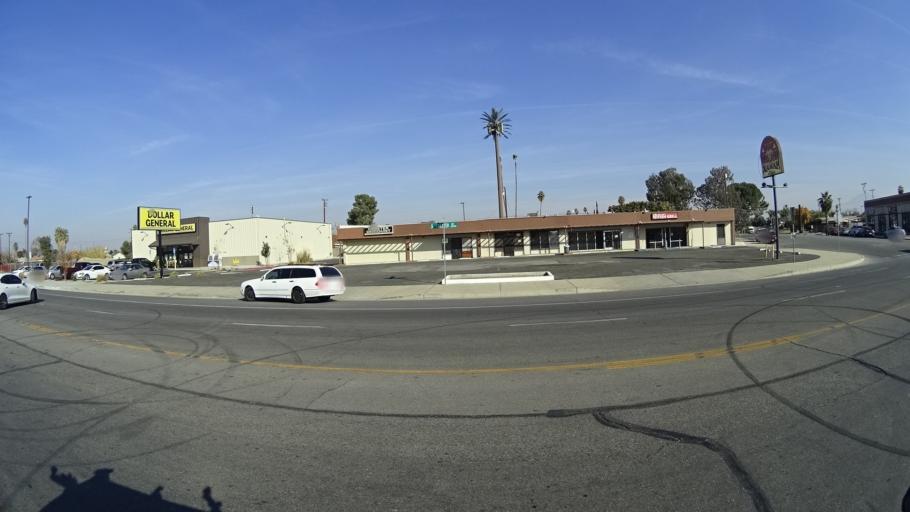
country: US
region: California
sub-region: Kern County
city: Bakersfield
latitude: 35.3291
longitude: -119.0122
